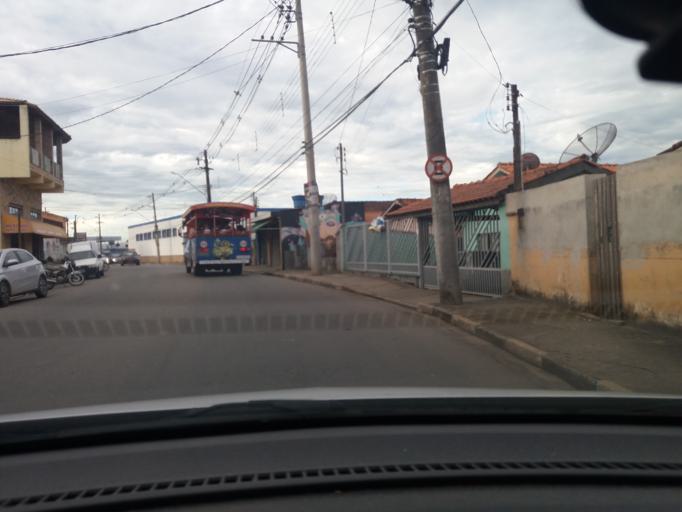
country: BR
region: Sao Paulo
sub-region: Bom Jesus Dos Perdoes
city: Bom Jesus dos Perdoes
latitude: -23.1292
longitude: -46.4671
